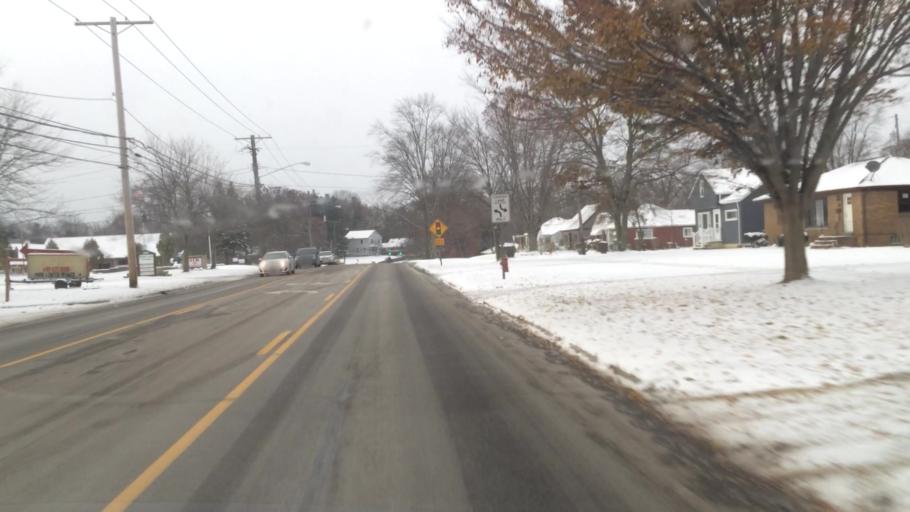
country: US
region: Ohio
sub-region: Cuyahoga County
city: Berea
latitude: 41.3821
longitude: -81.8576
